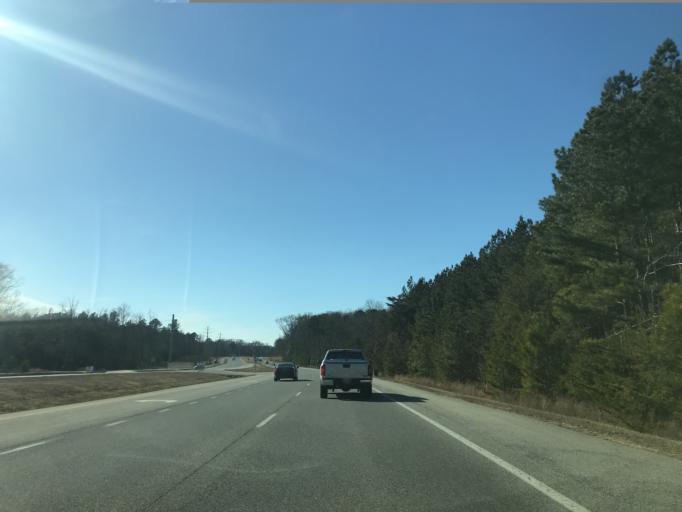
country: US
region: Maryland
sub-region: Charles County
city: Saint Charles
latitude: 38.5605
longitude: -76.9420
